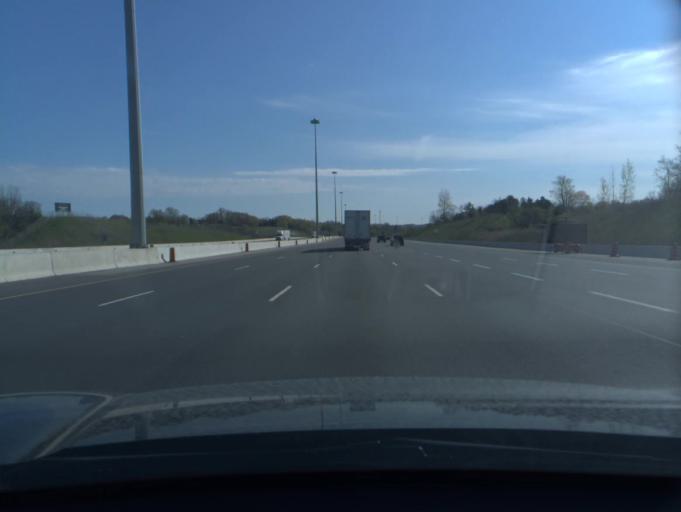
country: CA
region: Ontario
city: North Perth
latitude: 43.8151
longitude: -80.9998
